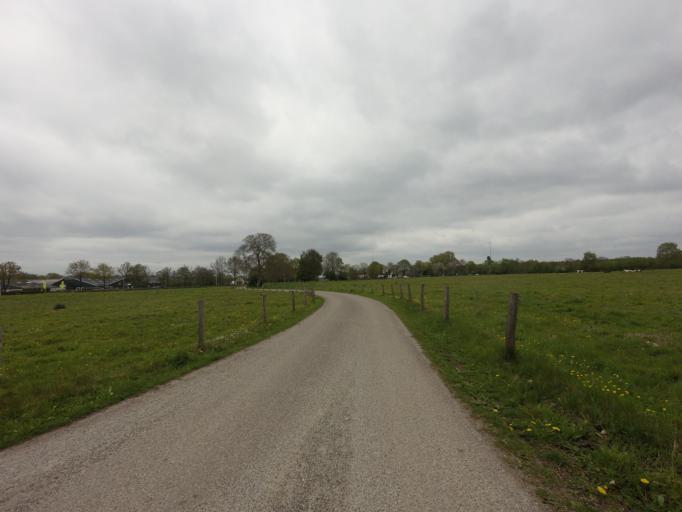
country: NL
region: Utrecht
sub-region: Gemeente De Bilt
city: De Bilt
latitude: 52.1379
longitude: 5.1754
